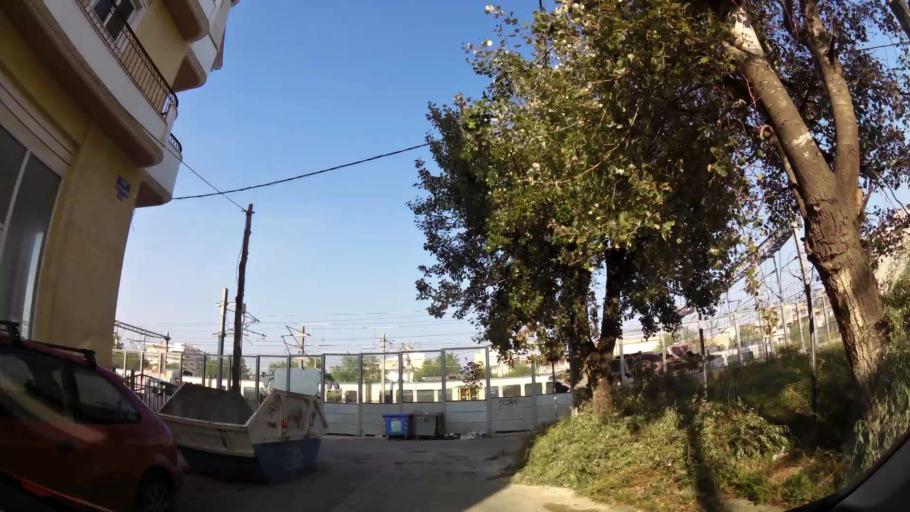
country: GR
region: Attica
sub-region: Nomarchia Dytikis Attikis
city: Zefyri
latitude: 38.0620
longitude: 23.7355
